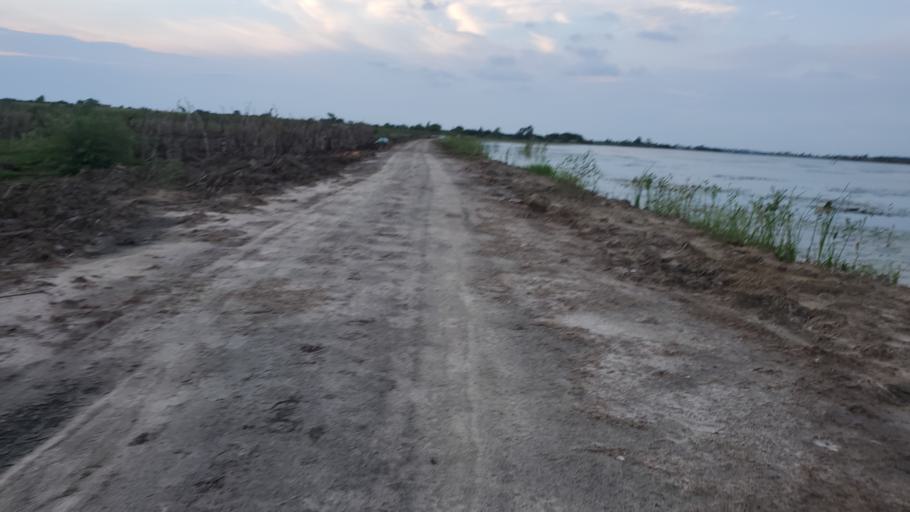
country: SN
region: Saint-Louis
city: Saint-Louis
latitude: 16.0327
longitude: -16.4142
